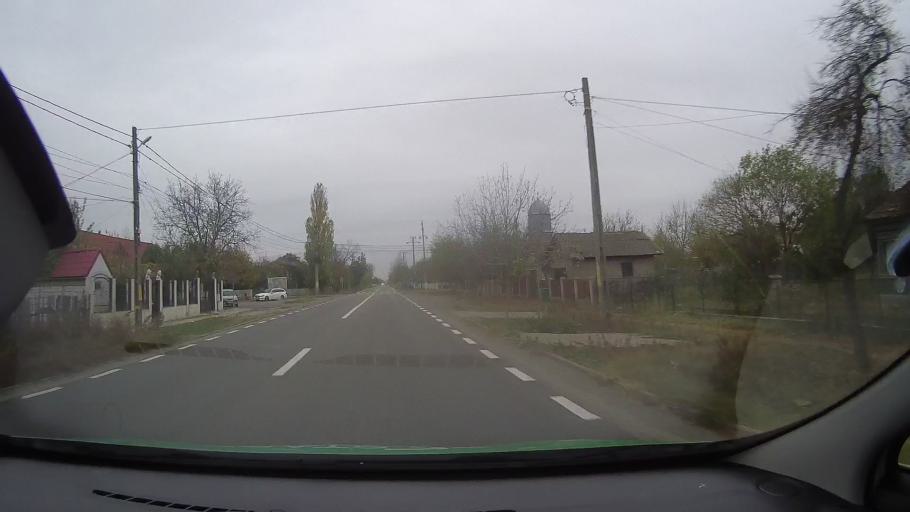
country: RO
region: Ialomita
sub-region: Comuna Slobozia
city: Slobozia
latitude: 44.6030
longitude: 27.3873
